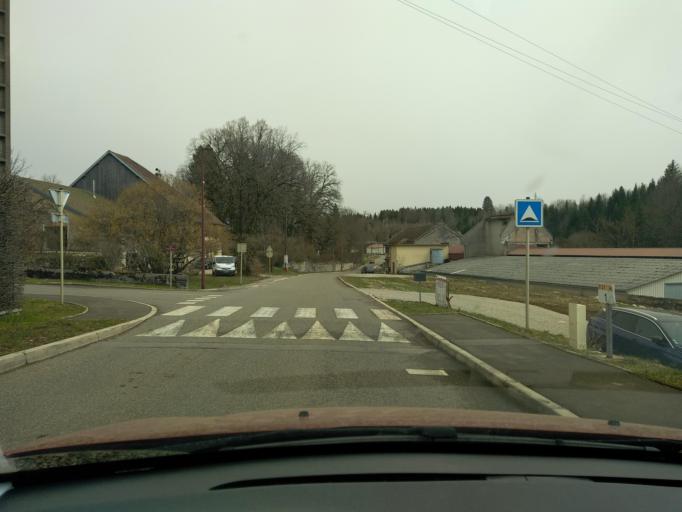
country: FR
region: Franche-Comte
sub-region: Departement du Jura
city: Champagnole
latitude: 46.7740
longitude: 5.8888
